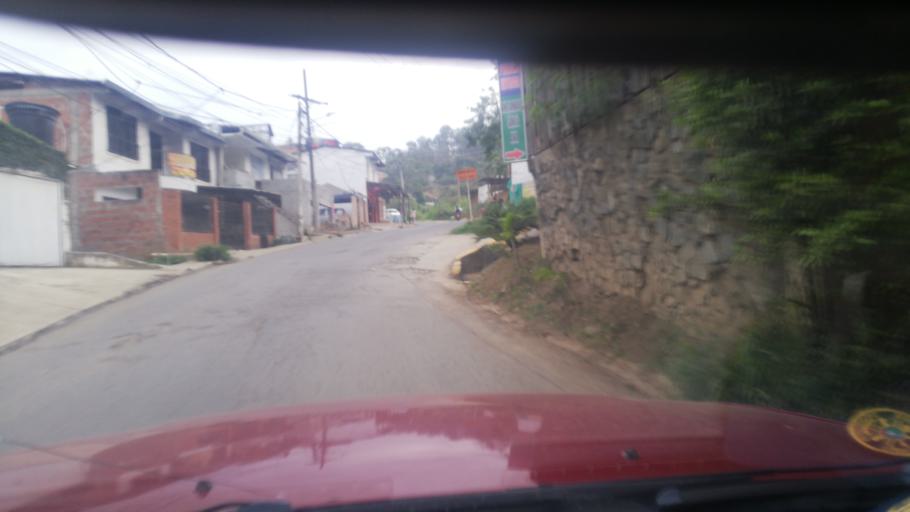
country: CO
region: Valle del Cauca
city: Cali
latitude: 3.4770
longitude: -76.5537
